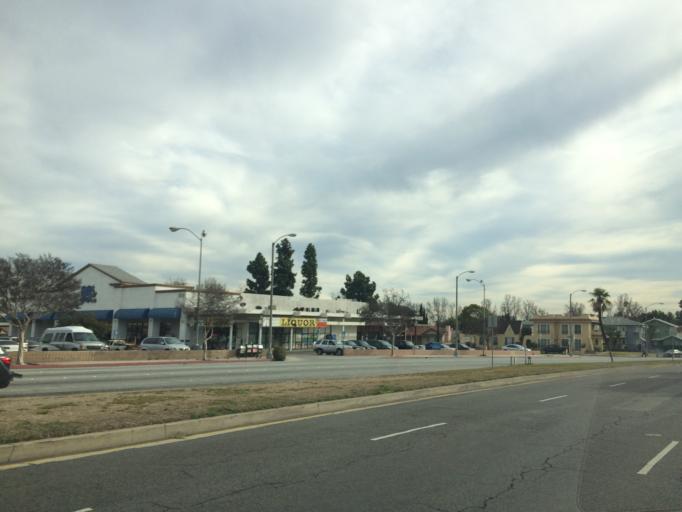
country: US
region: California
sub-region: Los Angeles County
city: South Pasadena
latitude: 34.0986
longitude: -118.1554
